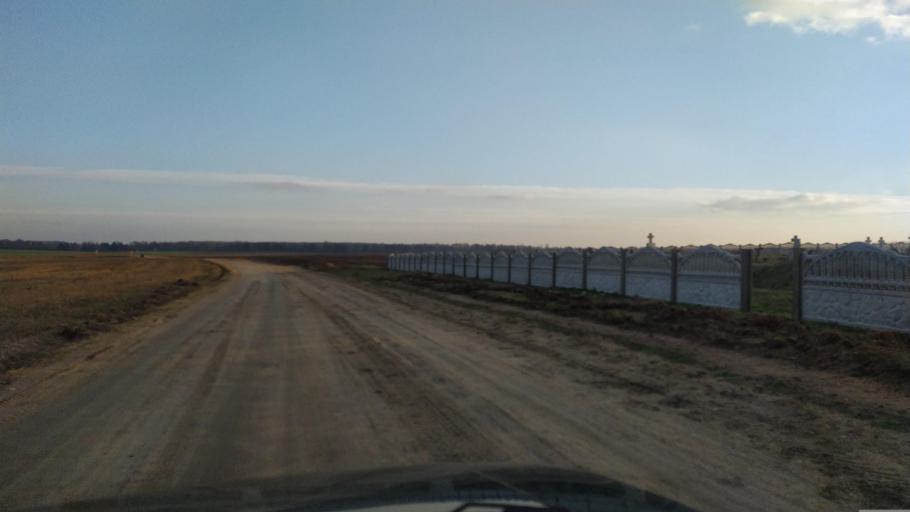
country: BY
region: Brest
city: Kamyanyets
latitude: 52.3826
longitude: 23.7842
